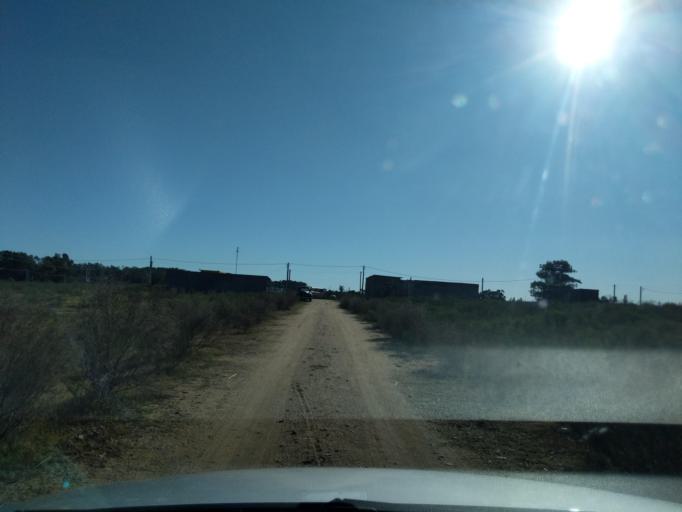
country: UY
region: Florida
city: Florida
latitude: -34.0828
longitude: -56.2401
